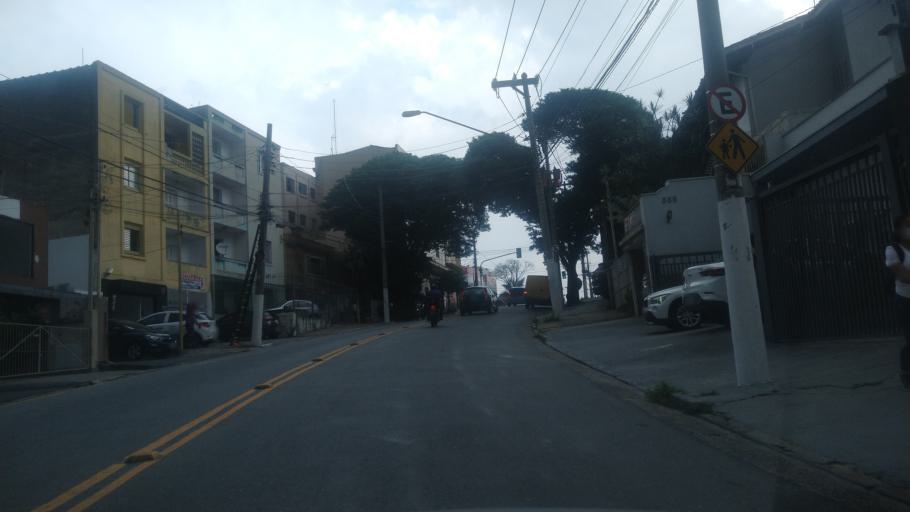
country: BR
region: Sao Paulo
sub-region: Sao Paulo
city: Sao Paulo
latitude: -23.4959
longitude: -46.6153
